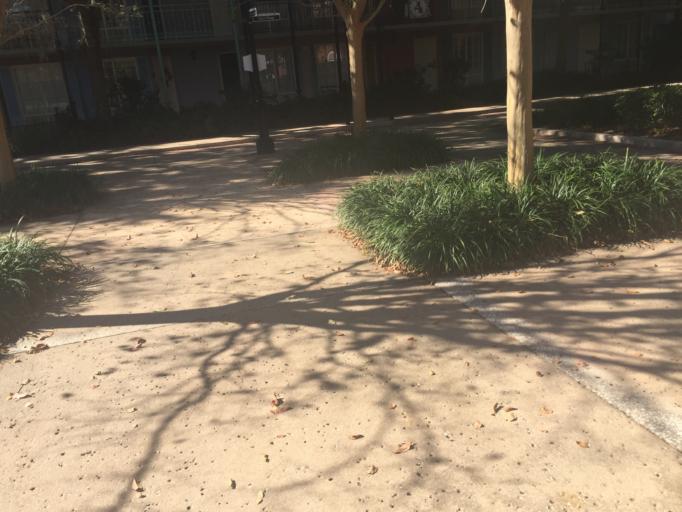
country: US
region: Florida
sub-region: Osceola County
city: Celebration
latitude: 28.3815
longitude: -81.5367
